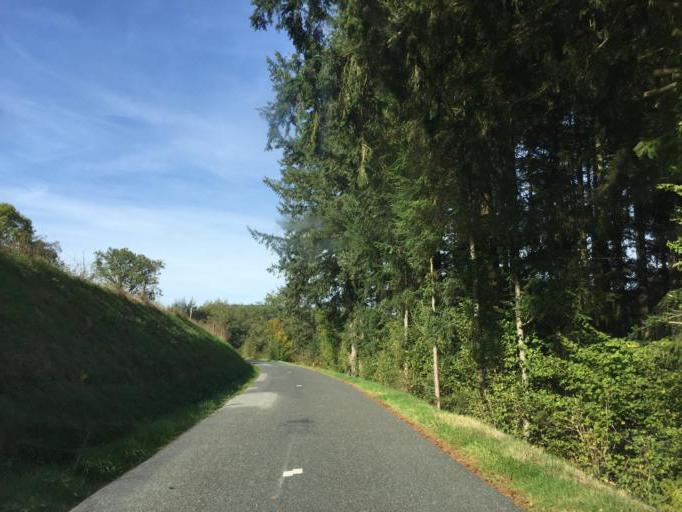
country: FR
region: Rhone-Alpes
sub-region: Departement de la Loire
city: Belmont-de-la-Loire
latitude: 46.1969
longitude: 4.4086
